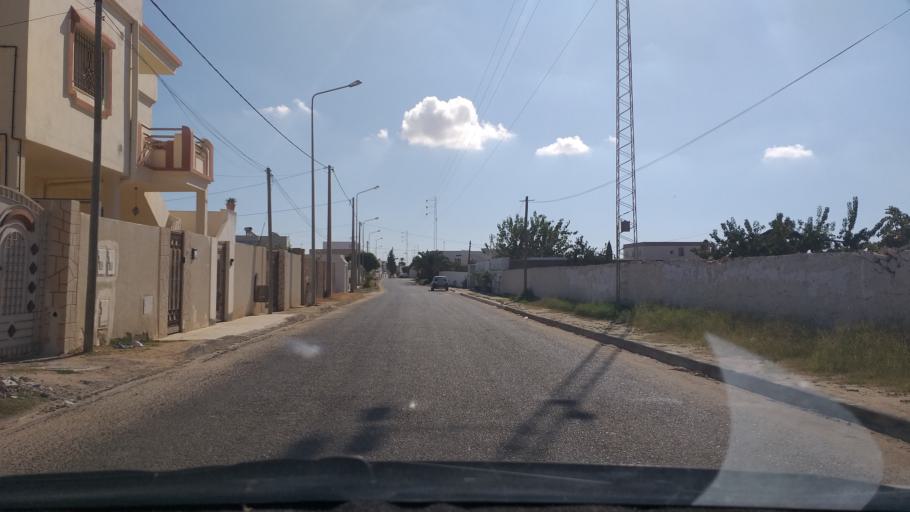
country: TN
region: Safaqis
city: Al Qarmadah
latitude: 34.8027
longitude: 10.7711
